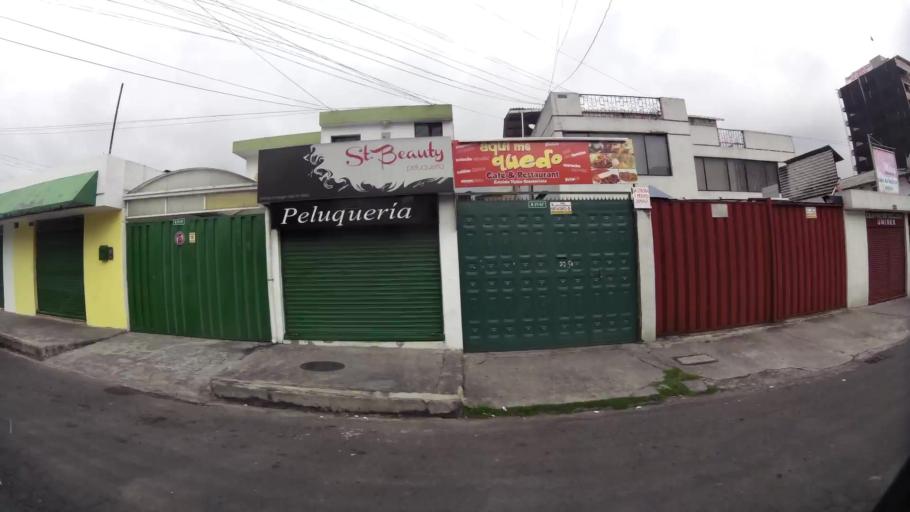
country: EC
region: Pichincha
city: Quito
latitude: -0.1915
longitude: -78.4894
